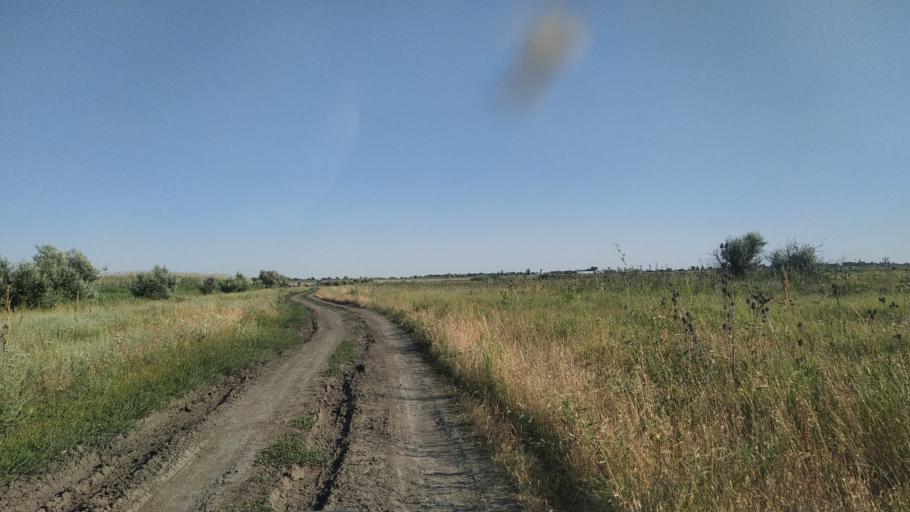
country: RU
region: Rostov
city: Kuleshovka
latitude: 47.1239
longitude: 39.6474
